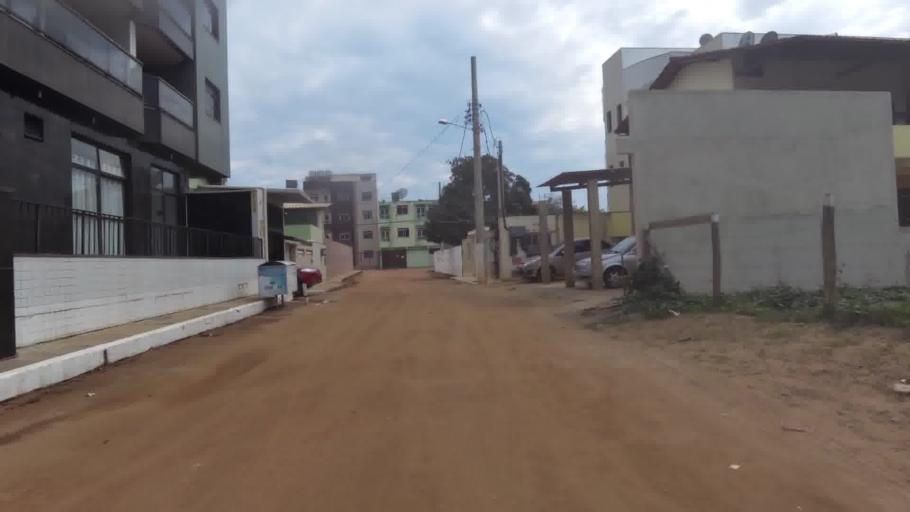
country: BR
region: Espirito Santo
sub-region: Piuma
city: Piuma
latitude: -20.8495
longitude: -40.7466
